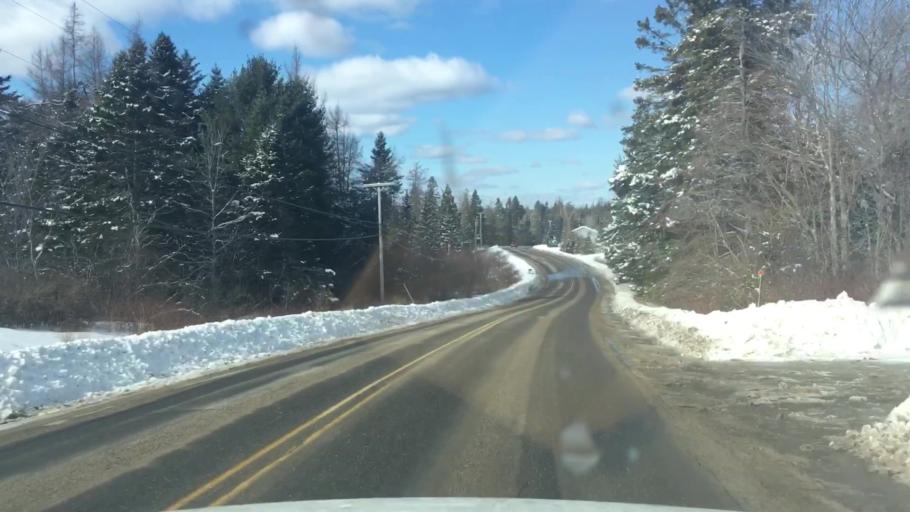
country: US
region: Maine
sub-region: Washington County
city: Machias
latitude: 44.6910
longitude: -67.4657
